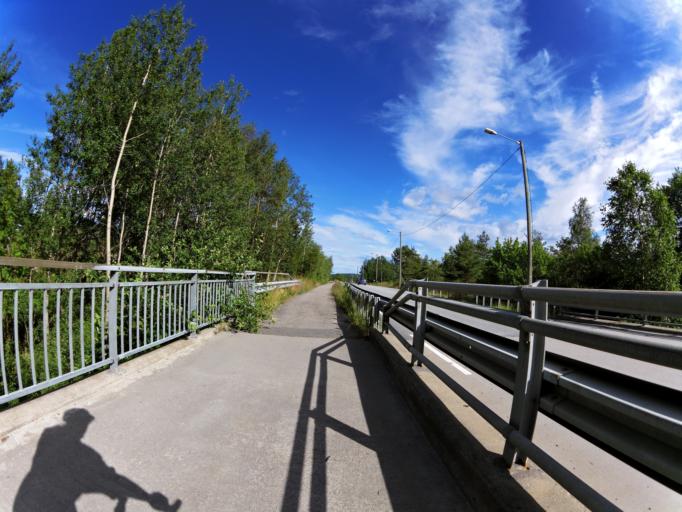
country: NO
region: Ostfold
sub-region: Fredrikstad
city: Fredrikstad
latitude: 59.2601
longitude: 11.0058
